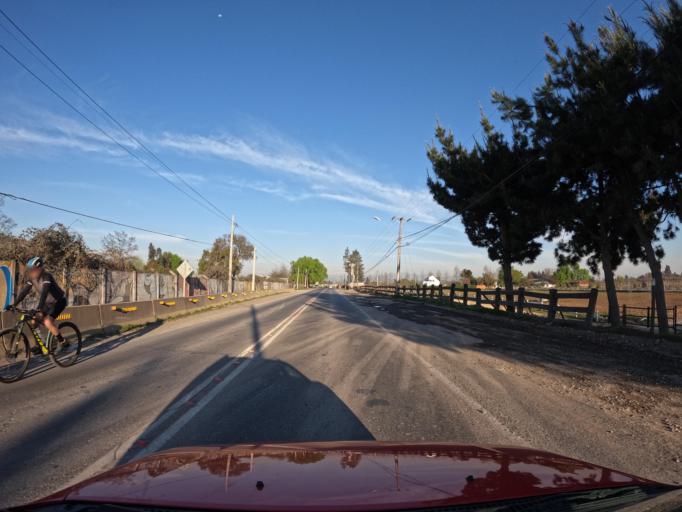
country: CL
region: Maule
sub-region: Provincia de Curico
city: Rauco
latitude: -34.9353
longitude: -71.2721
